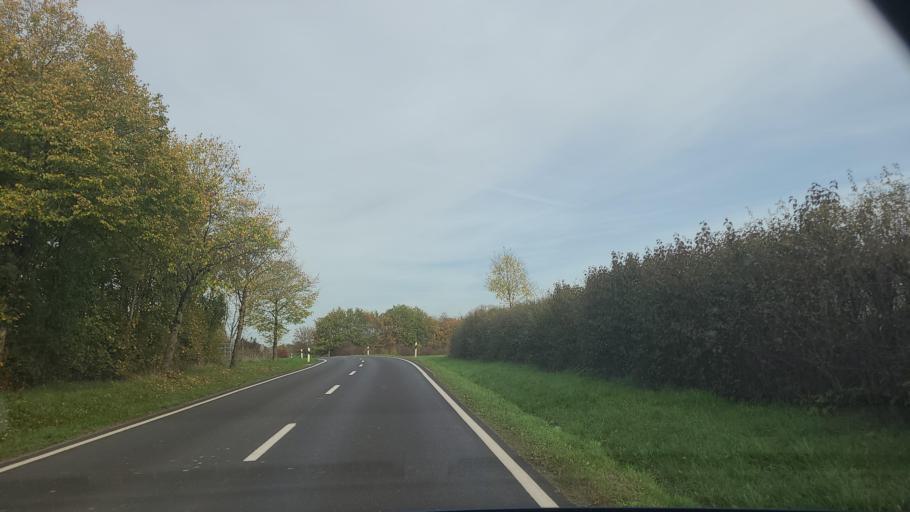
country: LU
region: Luxembourg
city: Hautcharage
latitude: 49.5848
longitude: 5.9107
